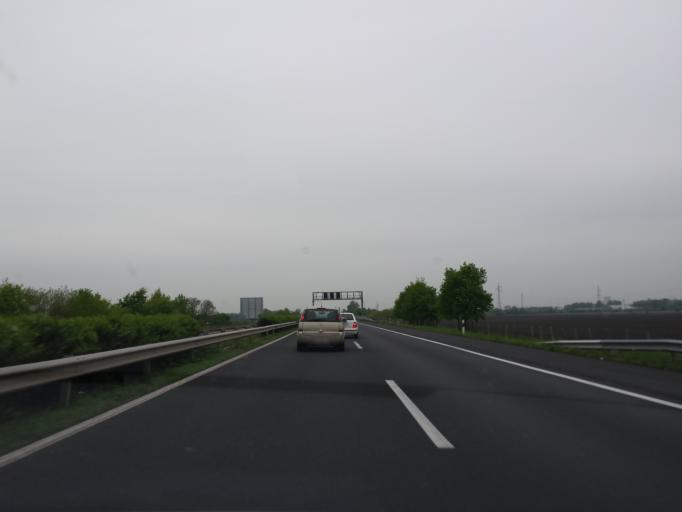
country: HU
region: Gyor-Moson-Sopron
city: Mosonmagyarovar
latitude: 47.8378
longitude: 17.2678
